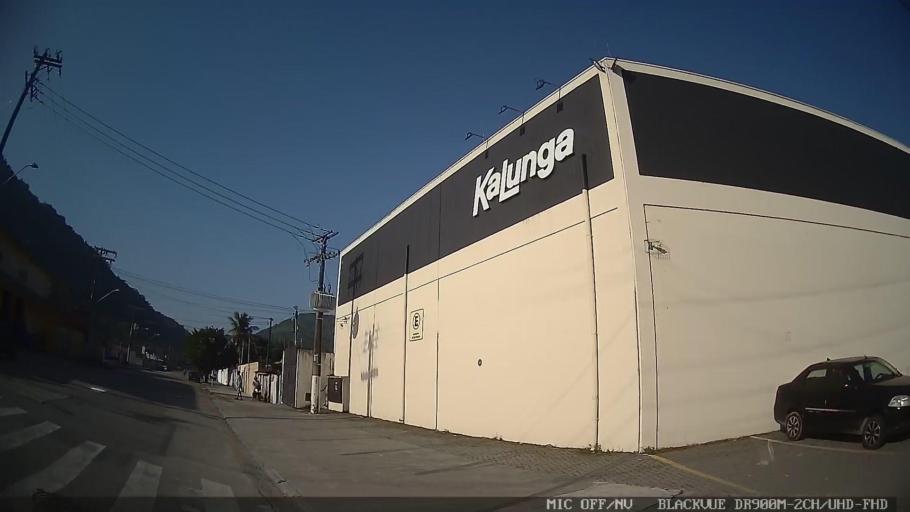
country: BR
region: Sao Paulo
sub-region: Guaruja
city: Guaruja
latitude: -23.9922
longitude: -46.2718
